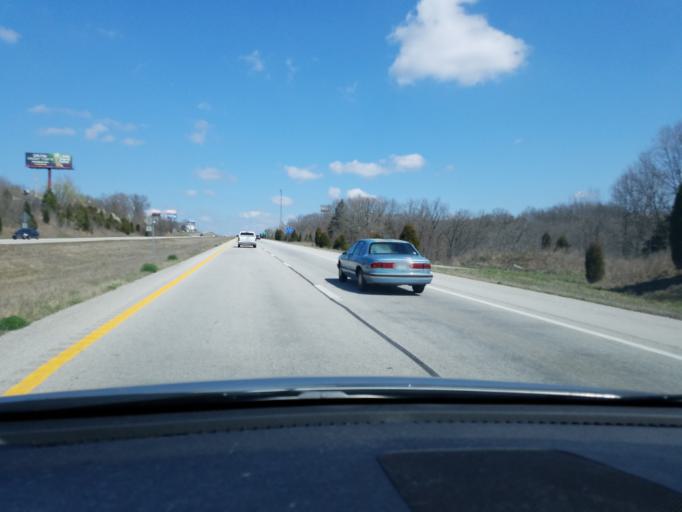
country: US
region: Missouri
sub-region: Taney County
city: Merriam Woods
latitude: 36.7992
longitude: -93.2264
